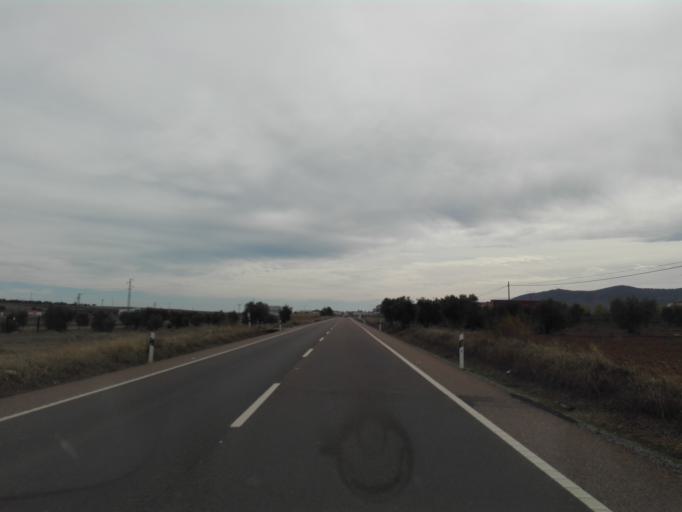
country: ES
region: Extremadura
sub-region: Provincia de Badajoz
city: Llerena
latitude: 38.2574
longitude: -6.0350
